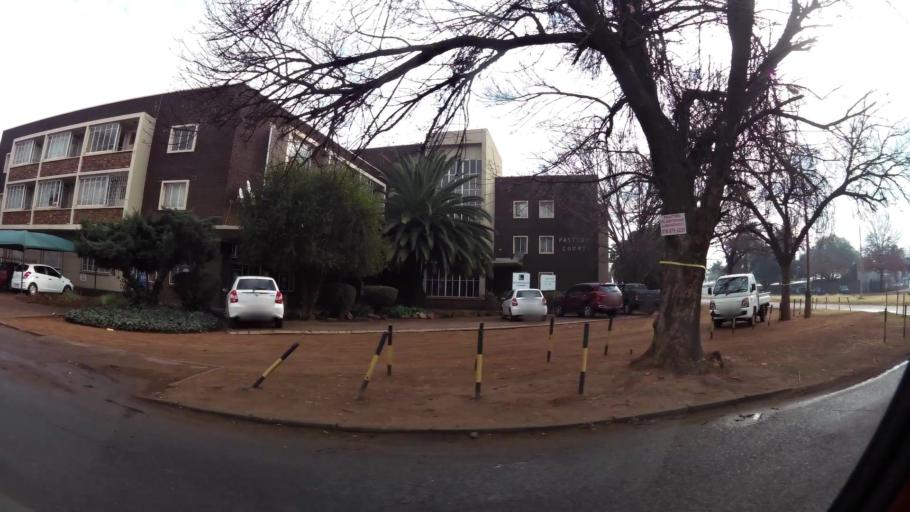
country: ZA
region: Gauteng
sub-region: Sedibeng District Municipality
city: Vanderbijlpark
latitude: -26.7030
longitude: 27.8313
